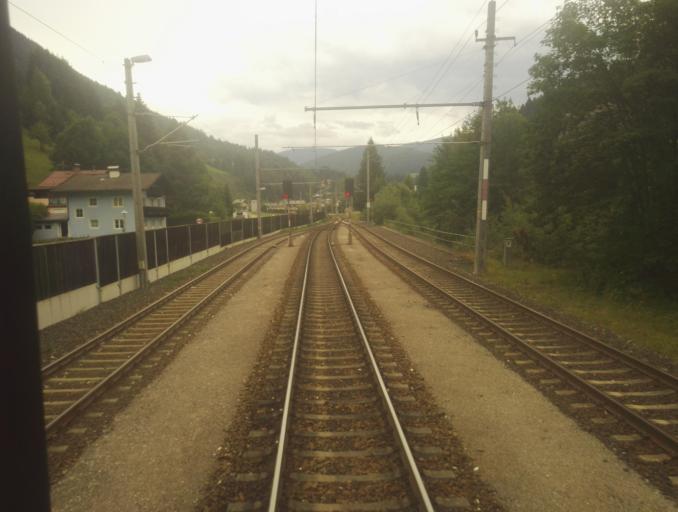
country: AT
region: Salzburg
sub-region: Politischer Bezirk Sankt Johann im Pongau
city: Huttau
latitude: 47.4182
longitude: 13.3255
